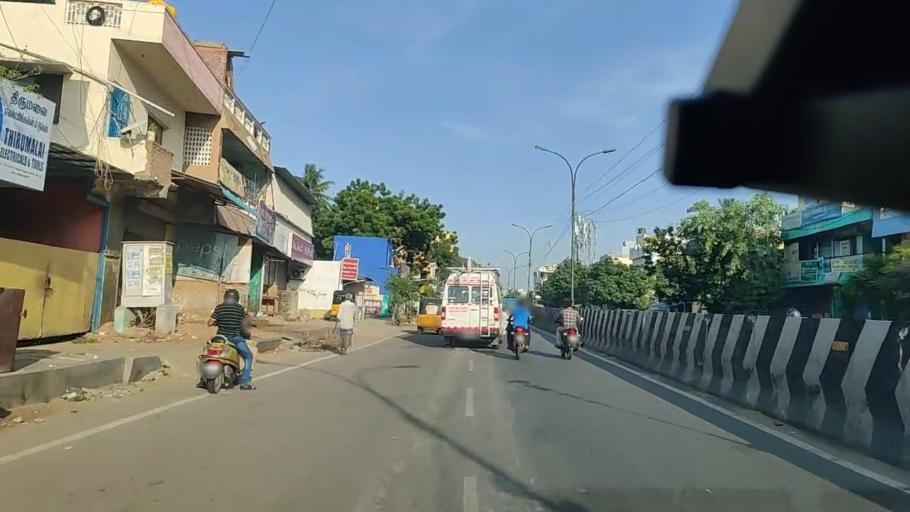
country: IN
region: Tamil Nadu
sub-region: Thiruvallur
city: Chinnasekkadu
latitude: 13.1219
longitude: 80.2516
